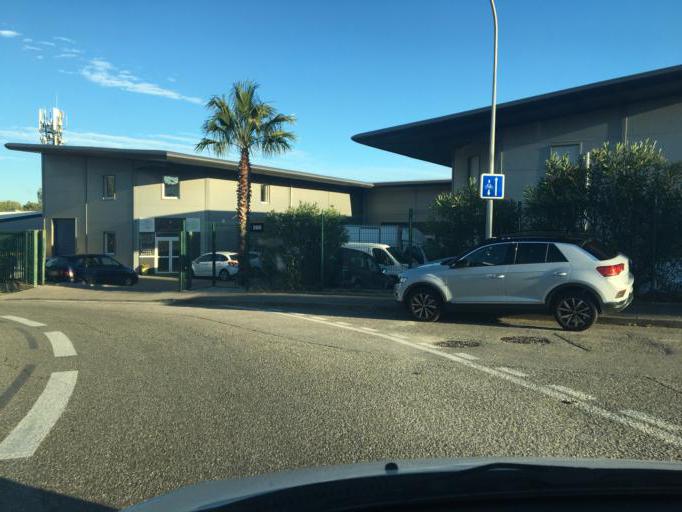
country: FR
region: Provence-Alpes-Cote d'Azur
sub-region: Departement des Bouches-du-Rhone
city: Ceyreste
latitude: 43.2060
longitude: 5.6078
